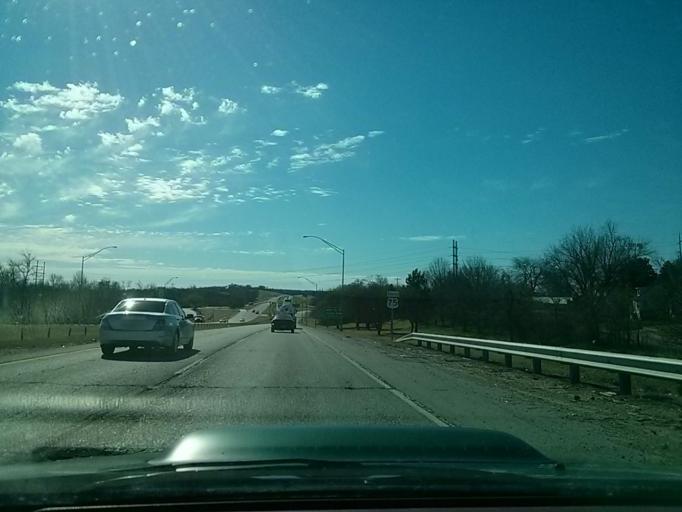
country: US
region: Oklahoma
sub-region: Tulsa County
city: Tulsa
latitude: 36.1104
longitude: -96.0121
